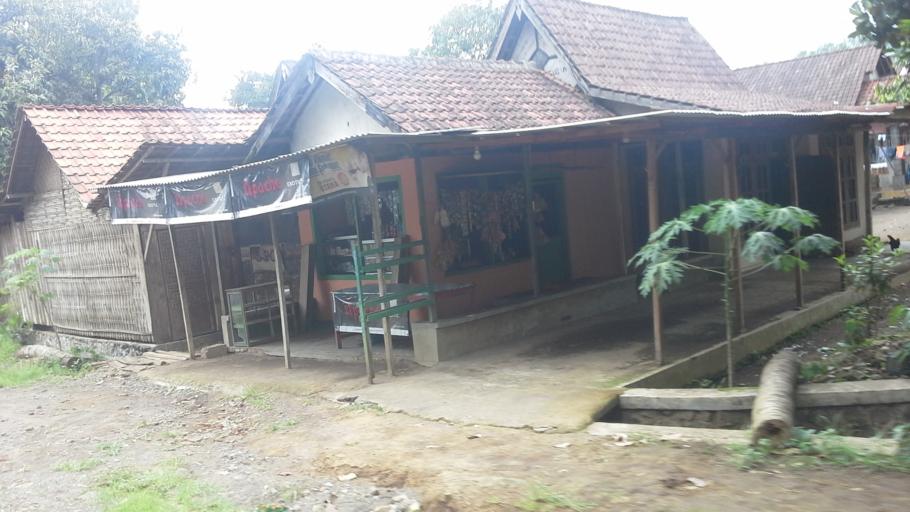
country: ID
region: East Java
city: Sumberpandan
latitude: -8.0000
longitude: 113.7861
